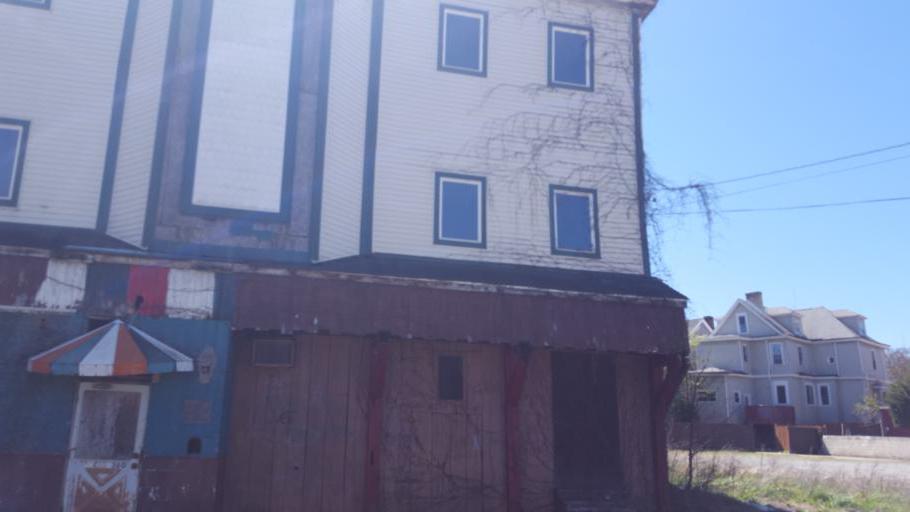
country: US
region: Ohio
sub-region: Belmont County
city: Bridgeport
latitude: 40.0708
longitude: -80.7307
